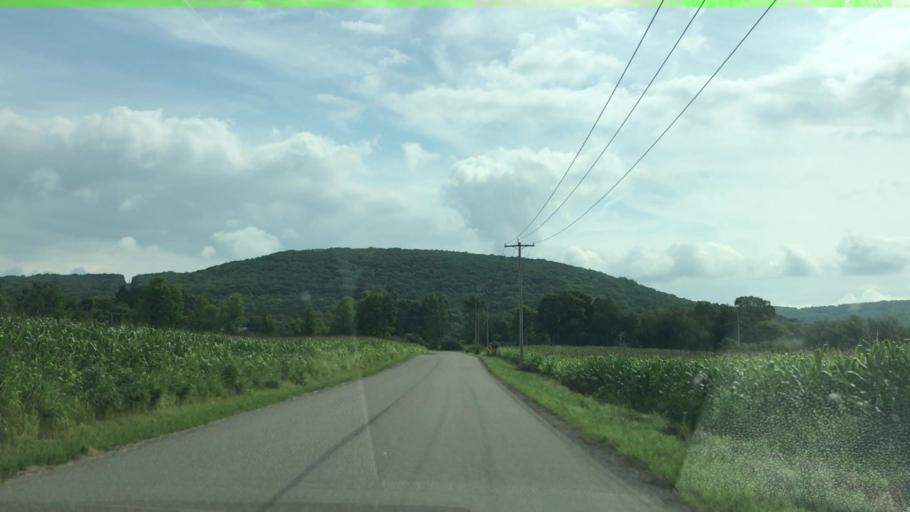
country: US
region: New York
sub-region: Ontario County
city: Naples
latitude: 42.5104
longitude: -77.2841
